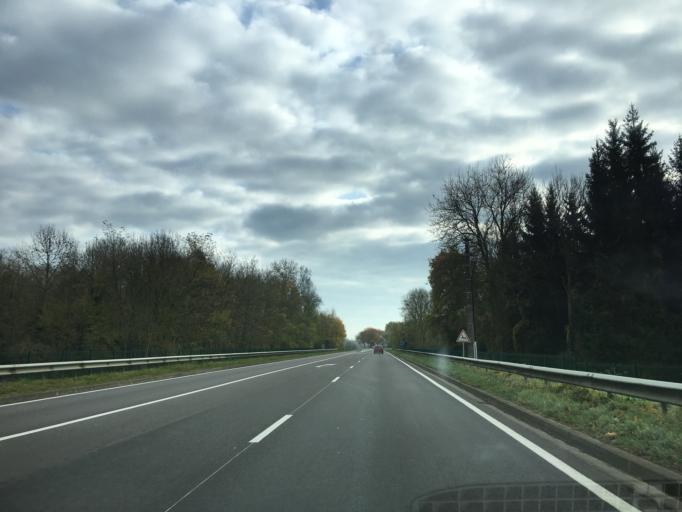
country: FR
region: Bourgogne
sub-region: Departement de l'Yonne
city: Pont-sur-Yonne
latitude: 48.2695
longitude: 3.2317
